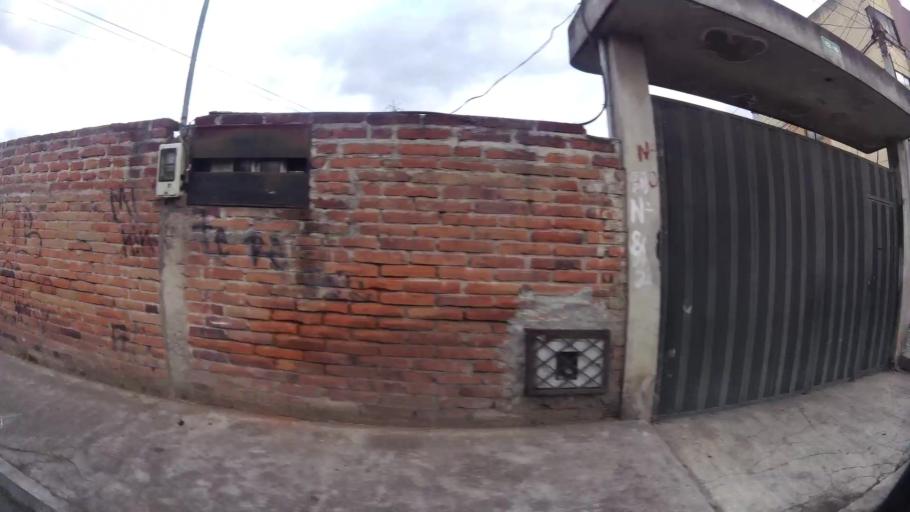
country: EC
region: Pichincha
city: Quito
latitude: -0.1477
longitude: -78.4598
